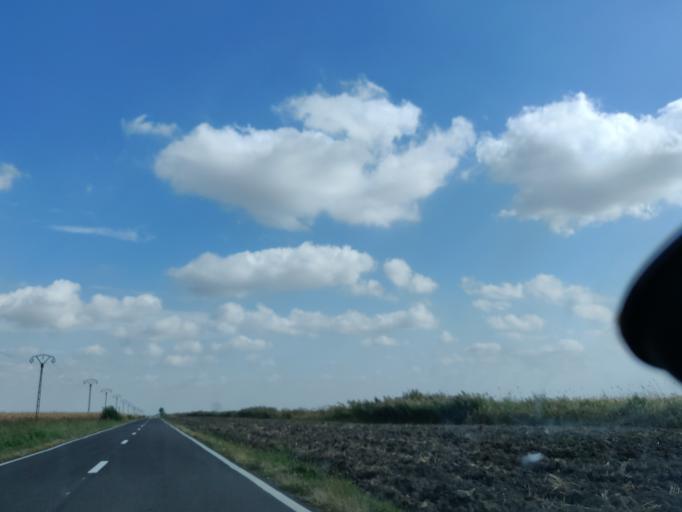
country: RO
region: Vrancea
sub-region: Comuna Maicanesti
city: Ramniceni
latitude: 45.4591
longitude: 27.4109
